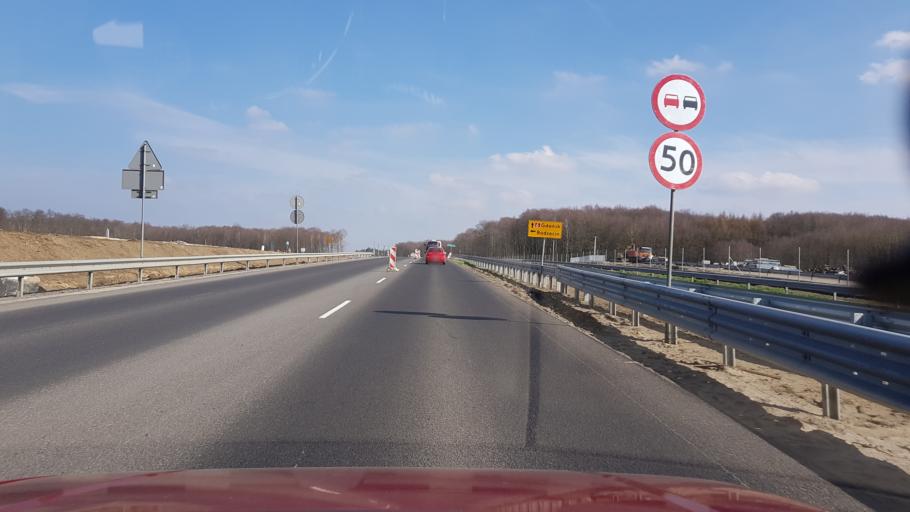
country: PL
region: West Pomeranian Voivodeship
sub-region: Powiat goleniowski
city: Mosty
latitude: 53.6158
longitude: 14.9287
